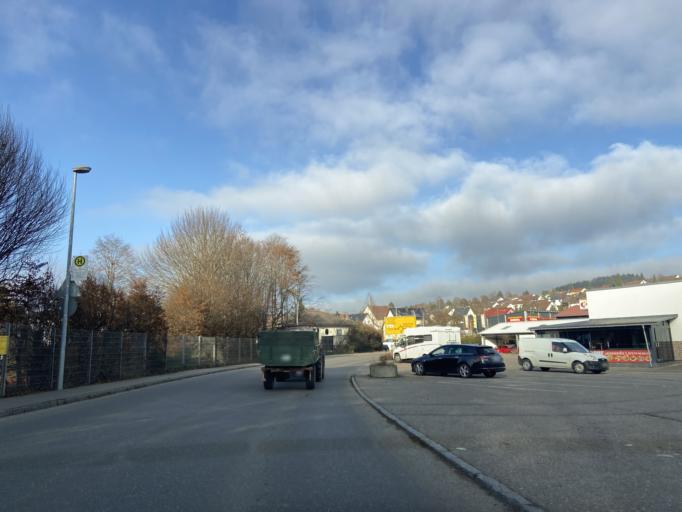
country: DE
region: Baden-Wuerttemberg
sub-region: Tuebingen Region
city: Gammertingen
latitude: 48.2451
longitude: 9.2218
